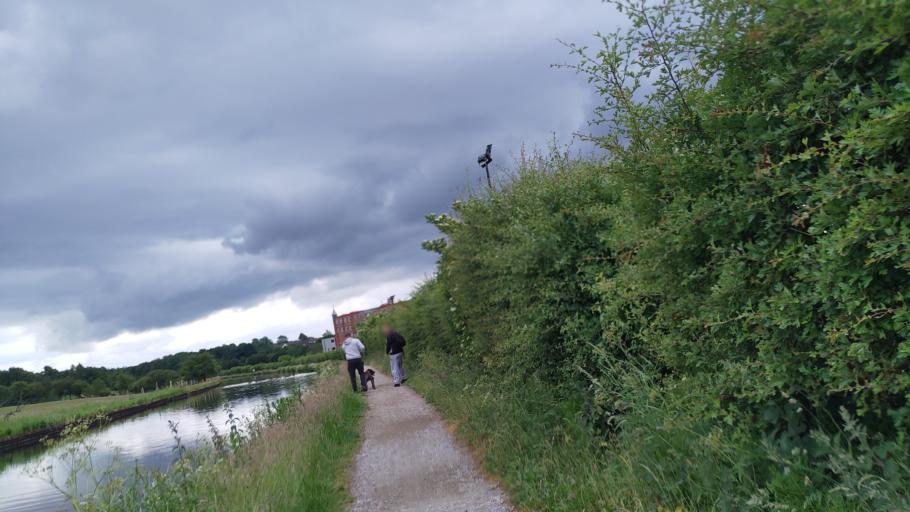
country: GB
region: England
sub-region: Lancashire
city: Chorley
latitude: 53.6702
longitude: -2.6208
